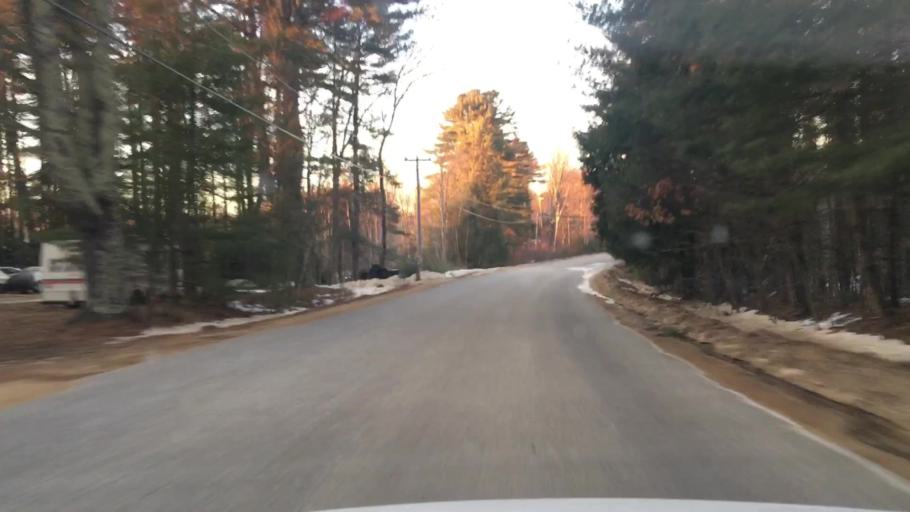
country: US
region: Maine
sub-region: York County
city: Lebanon
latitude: 43.3781
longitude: -70.8775
